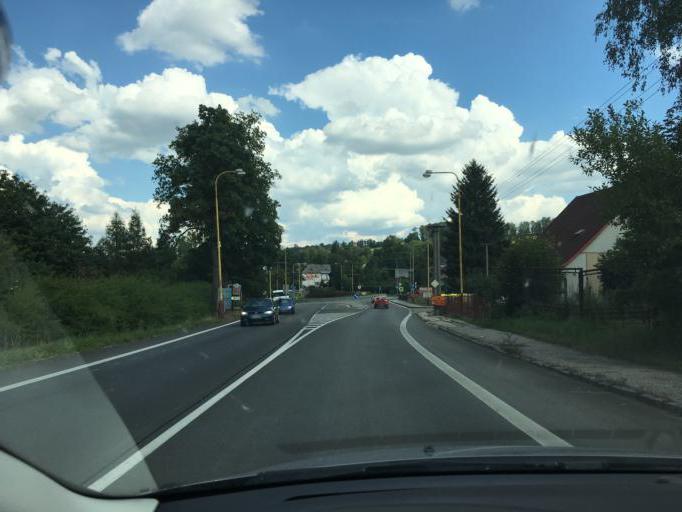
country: CZ
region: Liberecky
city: Jilemnice
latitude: 50.6224
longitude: 15.5055
